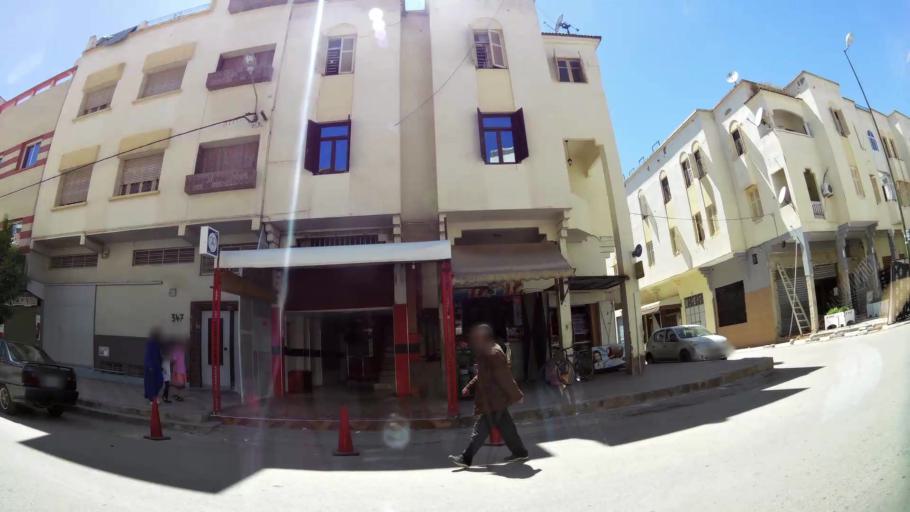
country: MA
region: Meknes-Tafilalet
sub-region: Meknes
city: Meknes
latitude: 33.8955
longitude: -5.5801
